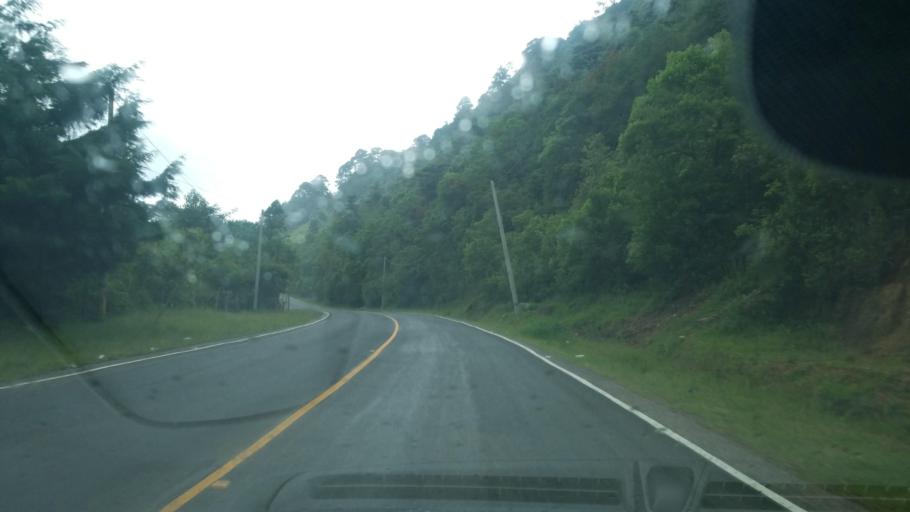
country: HN
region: Ocotepeque
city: La Labor
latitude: 14.4689
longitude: -89.0916
